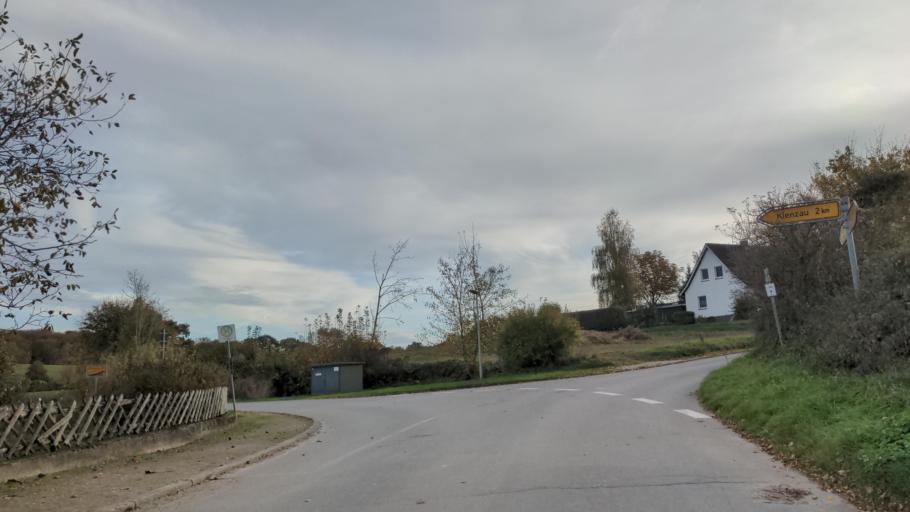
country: DE
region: Schleswig-Holstein
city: Glasau
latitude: 54.0867
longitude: 10.5487
